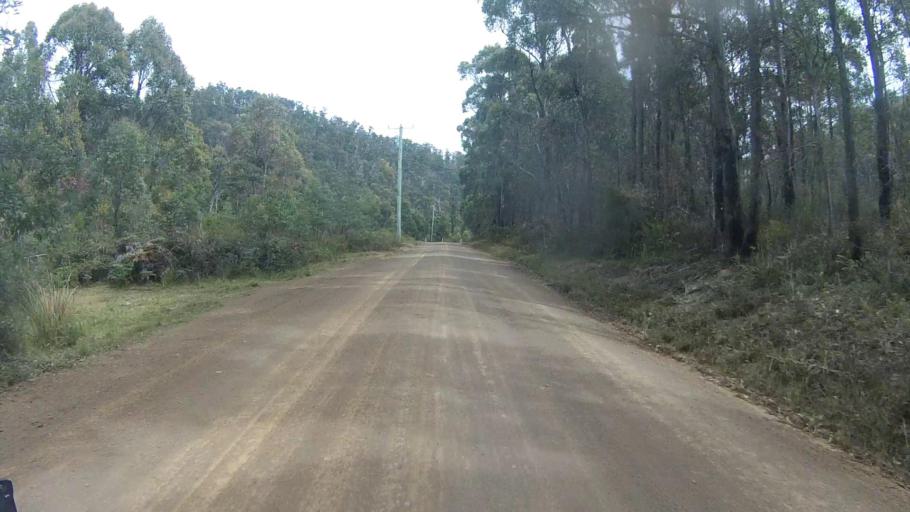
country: AU
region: Tasmania
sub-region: Sorell
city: Sorell
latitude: -42.7661
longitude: 147.8049
